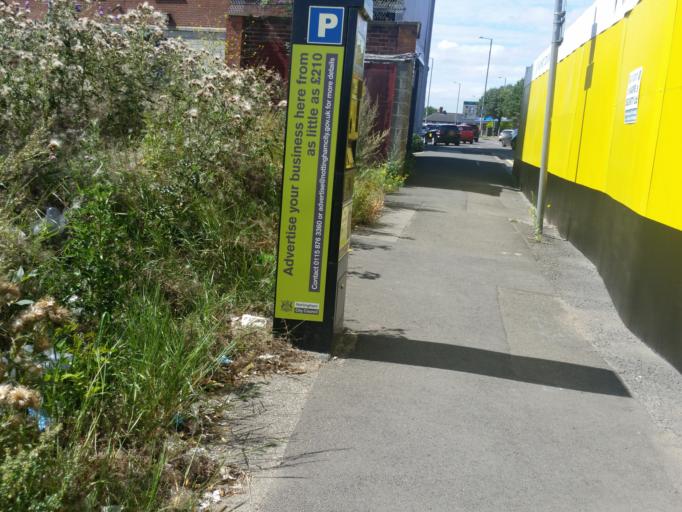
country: GB
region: England
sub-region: Nottingham
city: Nottingham
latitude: 52.9506
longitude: -1.1383
